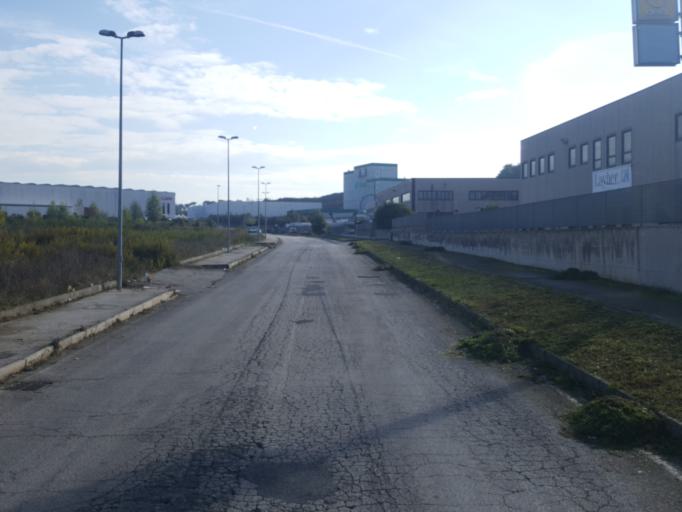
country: IT
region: Latium
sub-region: Citta metropolitana di Roma Capitale
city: Colleferro
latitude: 41.7555
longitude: 12.9910
